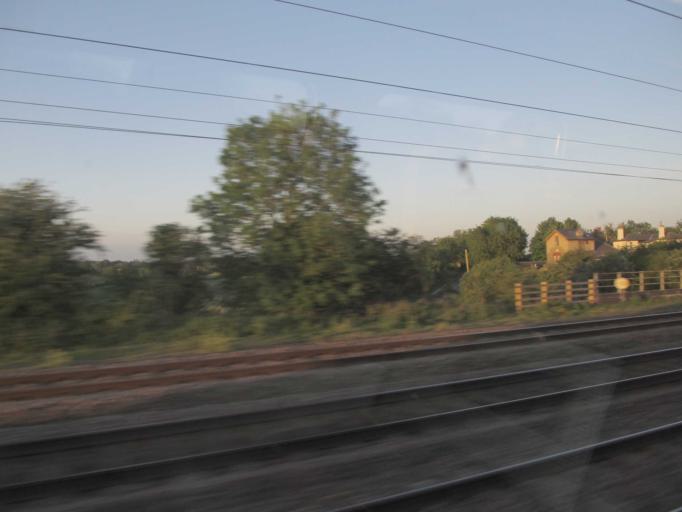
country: GB
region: England
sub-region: District of Rutland
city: Clipsham
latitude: 52.8088
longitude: -0.5394
